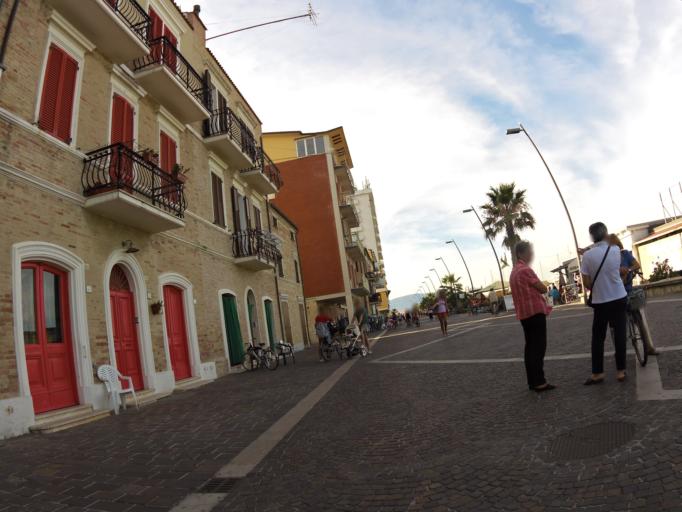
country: IT
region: The Marches
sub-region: Provincia di Macerata
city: Porto Recanati
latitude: 43.4340
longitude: 13.6649
